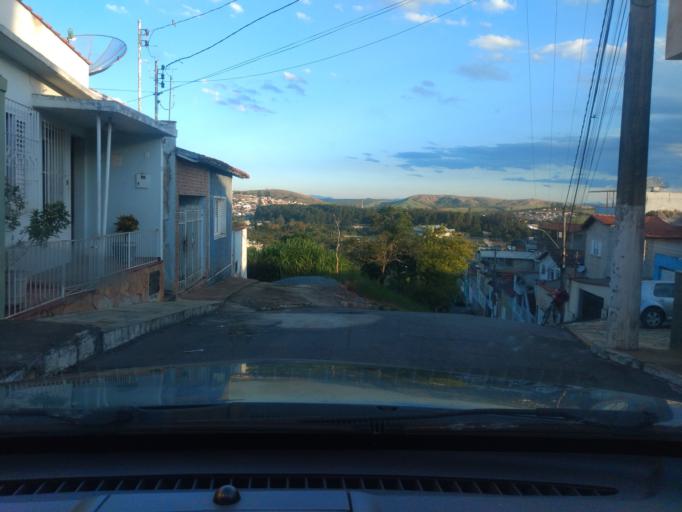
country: BR
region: Minas Gerais
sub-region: Tres Coracoes
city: Tres Coracoes
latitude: -21.6962
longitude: -45.2513
